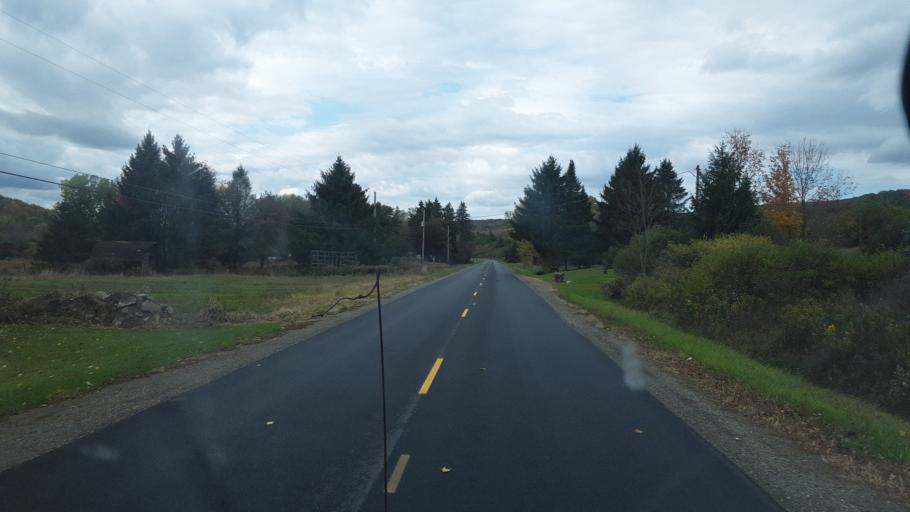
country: US
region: New York
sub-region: Allegany County
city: Alfred
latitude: 42.3684
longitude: -77.7885
